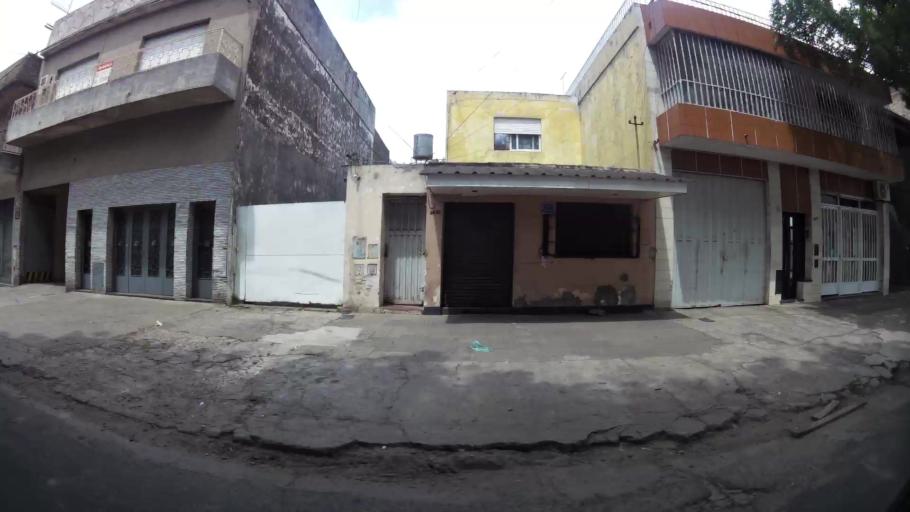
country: AR
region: Santa Fe
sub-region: Departamento de Rosario
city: Rosario
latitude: -32.9781
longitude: -60.6548
